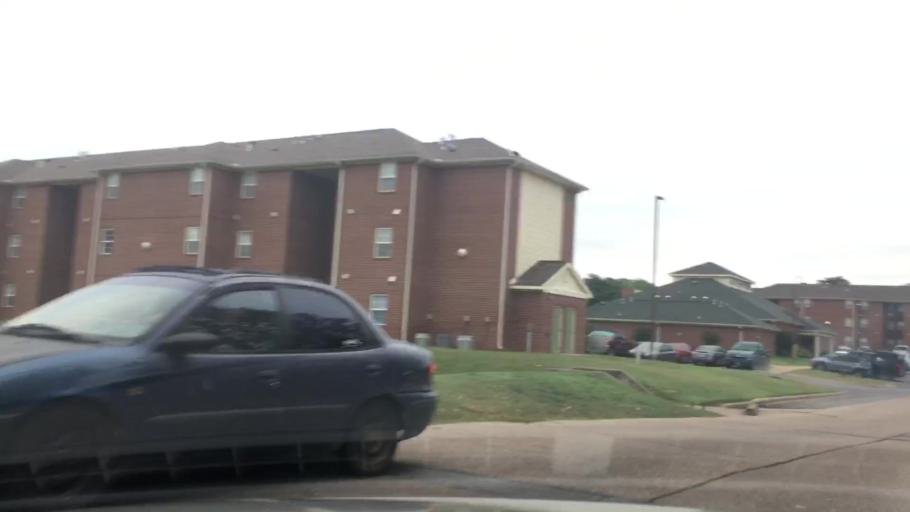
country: US
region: Oklahoma
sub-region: Cherokee County
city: Tahlequah
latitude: 35.9236
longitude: -94.9695
